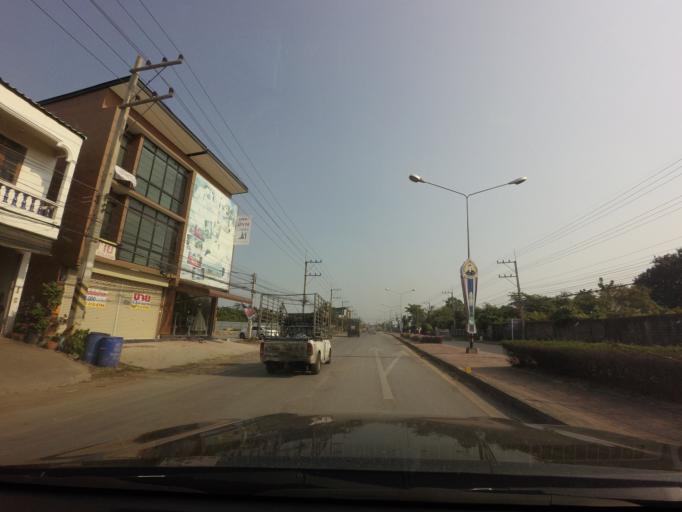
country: TH
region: Kanchanaburi
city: Tha Maka
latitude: 13.8891
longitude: 99.7994
